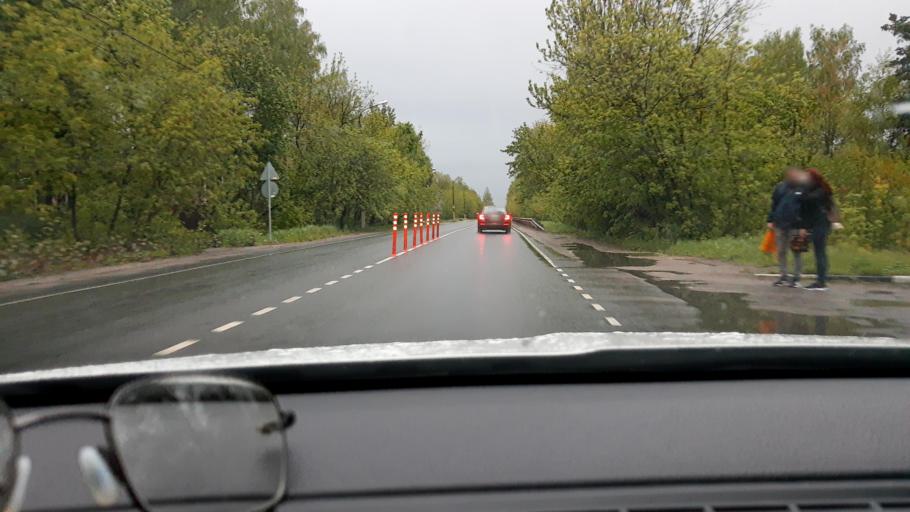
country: RU
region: Moskovskaya
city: Zagoryanskiy
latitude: 55.9270
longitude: 37.9182
